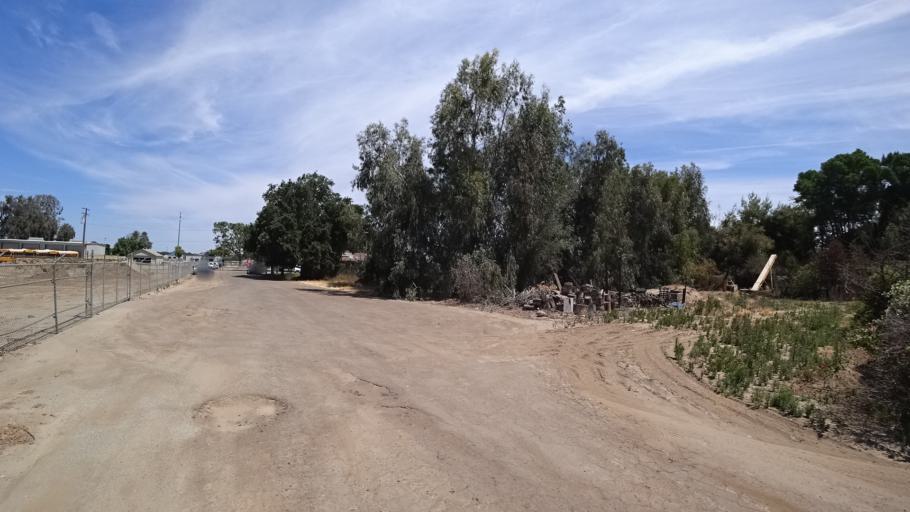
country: US
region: California
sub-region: Kings County
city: Armona
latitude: 36.3442
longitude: -119.7102
